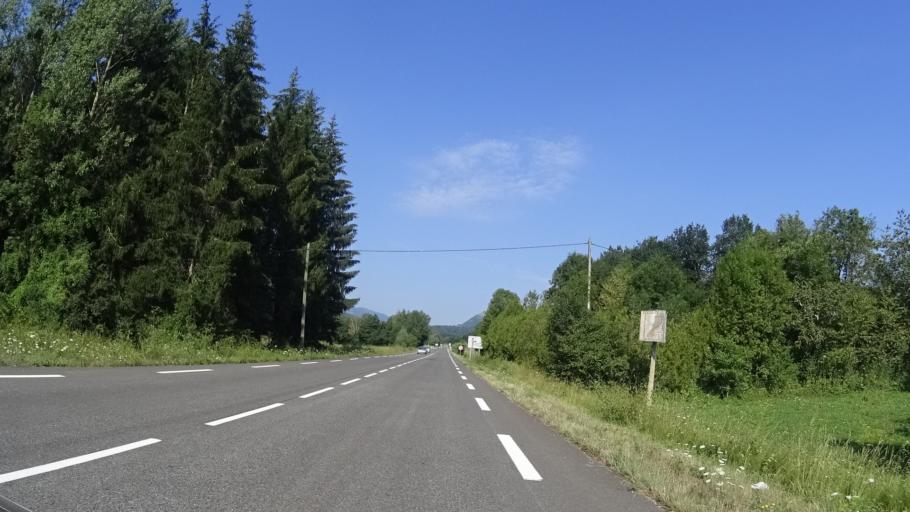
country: FR
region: Midi-Pyrenees
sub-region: Departement de l'Ariege
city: Saint-Paul-de-Jarrat
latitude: 42.9324
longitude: 1.7287
